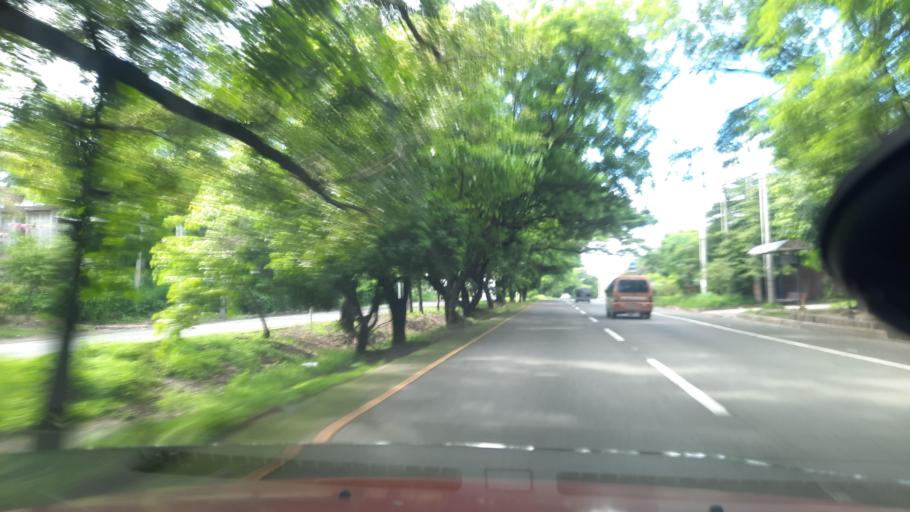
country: SV
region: La Paz
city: Olocuilta
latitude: 13.5455
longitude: -89.1135
